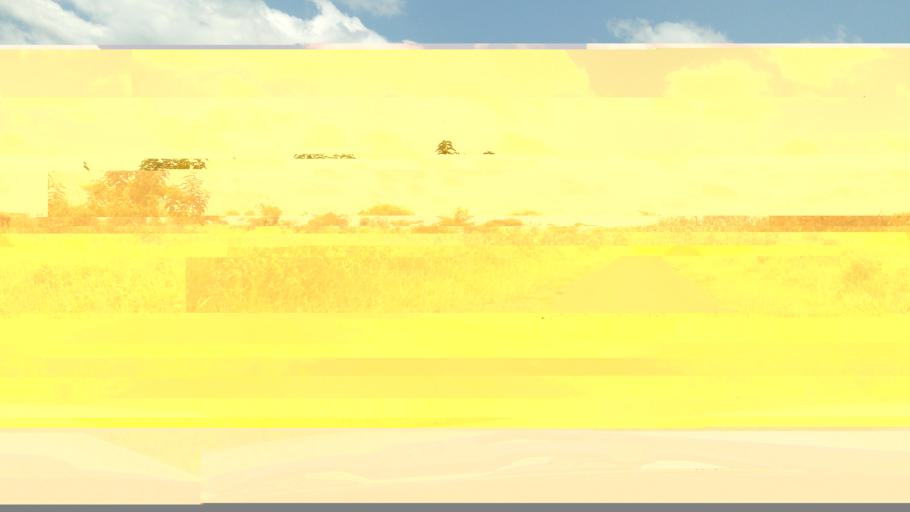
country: UG
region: Western Region
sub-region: Masindi District
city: Masindi
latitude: 1.7388
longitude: 31.8757
